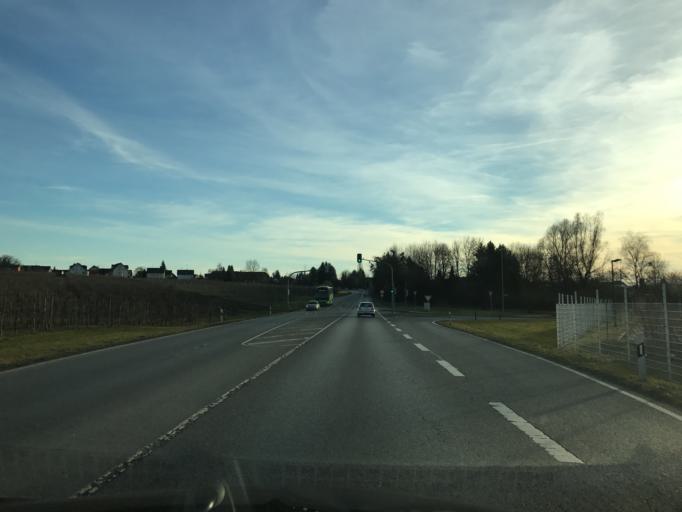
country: DE
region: Baden-Wuerttemberg
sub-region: Tuebingen Region
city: Ravensburg
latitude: 47.7546
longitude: 9.6004
